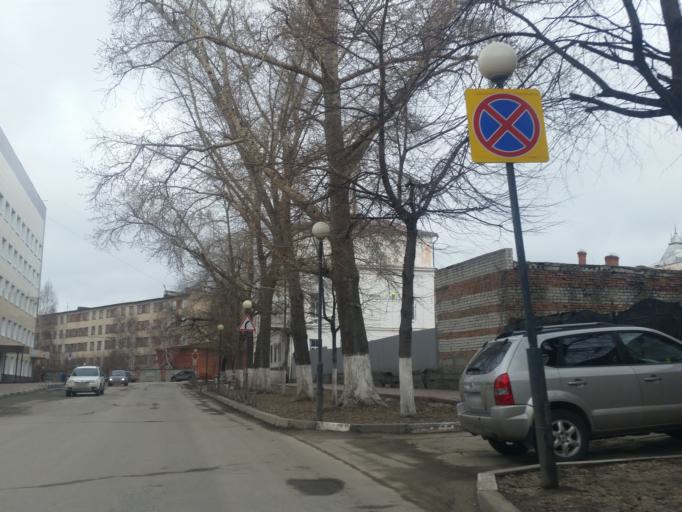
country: RU
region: Ulyanovsk
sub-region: Ulyanovskiy Rayon
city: Ulyanovsk
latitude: 54.3126
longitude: 48.4011
